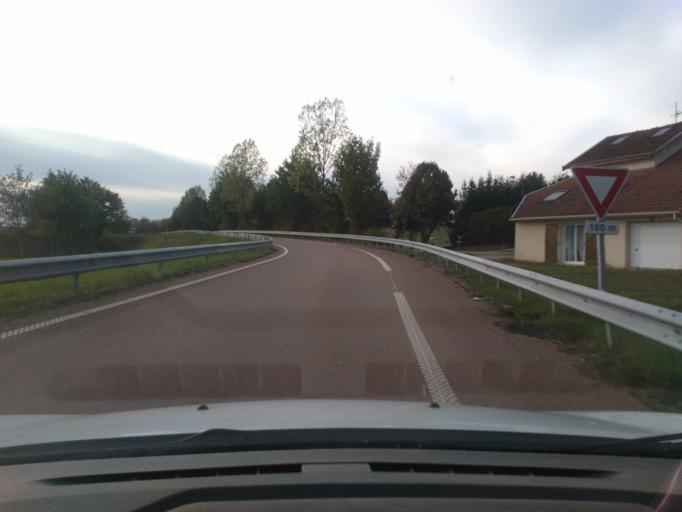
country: FR
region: Lorraine
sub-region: Departement des Vosges
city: Darnieulles
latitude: 48.2199
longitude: 6.2460
